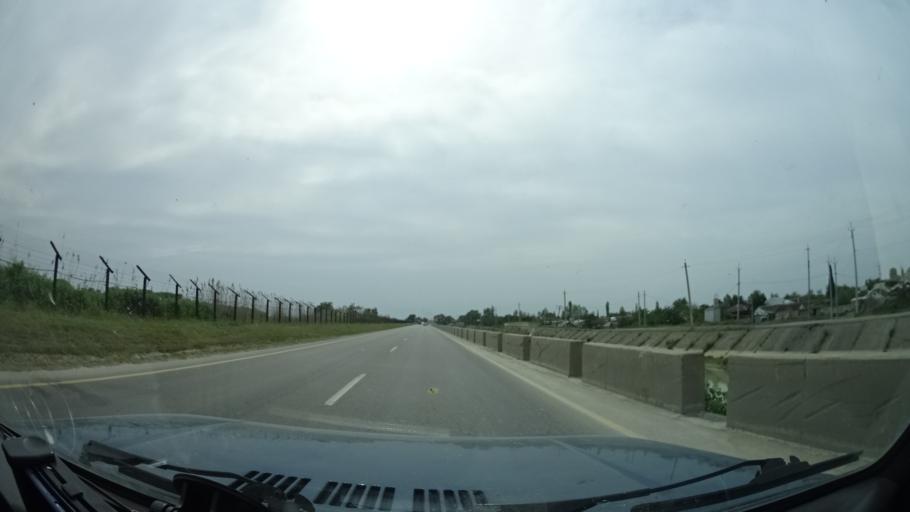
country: IR
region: Ardabil
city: Parsabad
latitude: 39.7366
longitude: 47.9604
